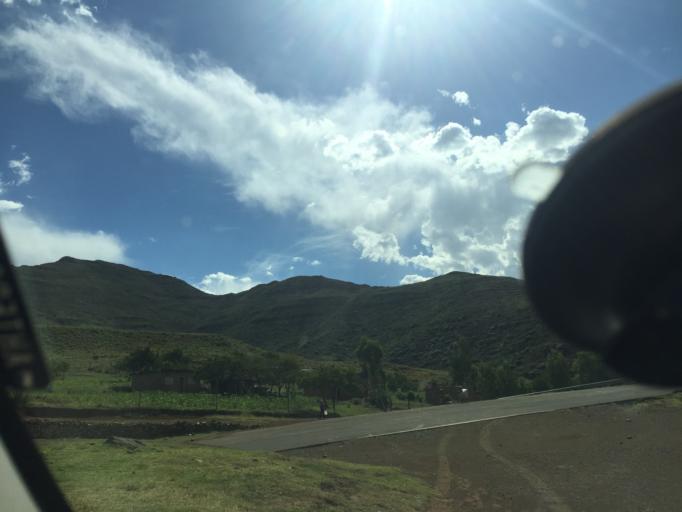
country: LS
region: Maseru
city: Nako
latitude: -29.5921
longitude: 27.7521
